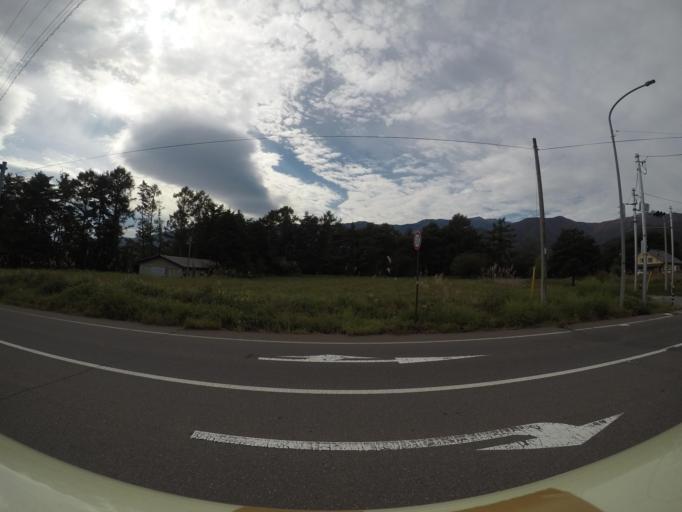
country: JP
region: Nagano
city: Ina
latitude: 35.8619
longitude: 137.8955
